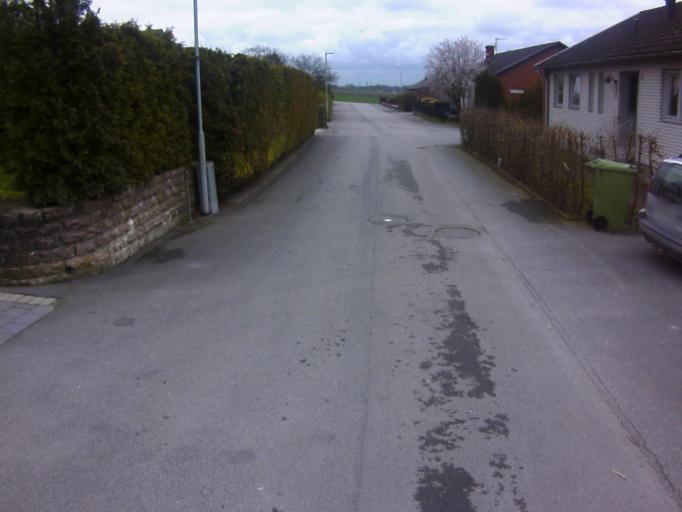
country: SE
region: Skane
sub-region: Lunds Kommun
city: Lund
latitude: 55.7910
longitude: 13.2062
